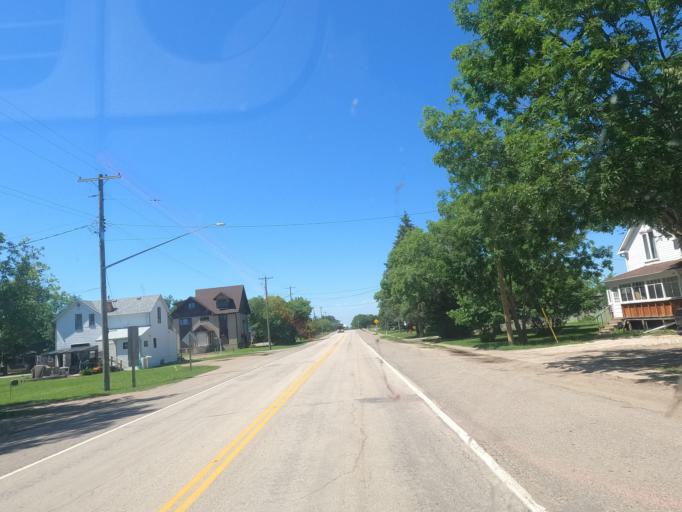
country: CA
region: Manitoba
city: Souris
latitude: 49.6209
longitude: -100.2630
